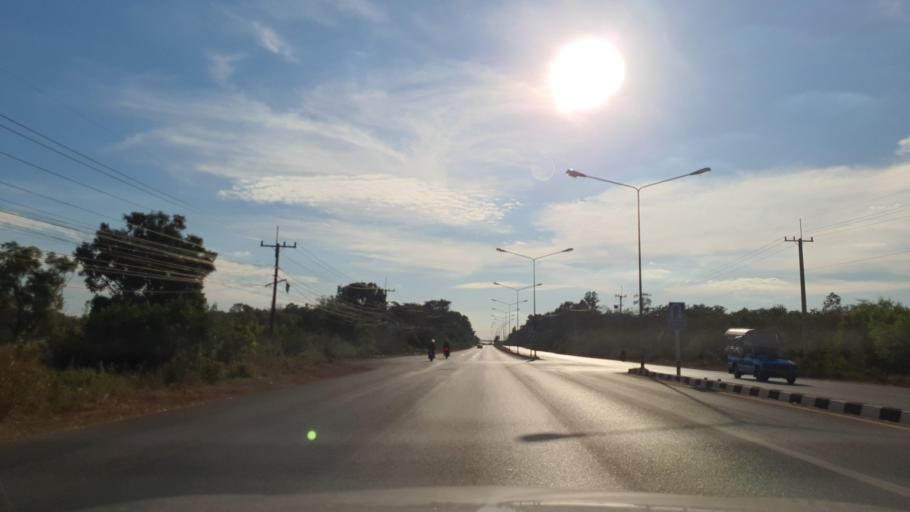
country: TH
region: Maha Sarakham
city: Kantharawichai
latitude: 16.3353
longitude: 103.3084
